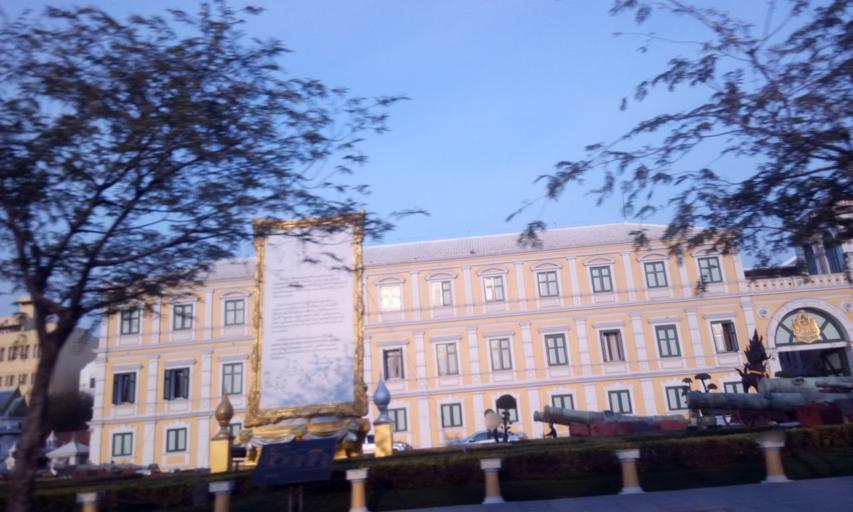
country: TH
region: Bangkok
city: Bangkok
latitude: 13.7521
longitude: 100.4936
